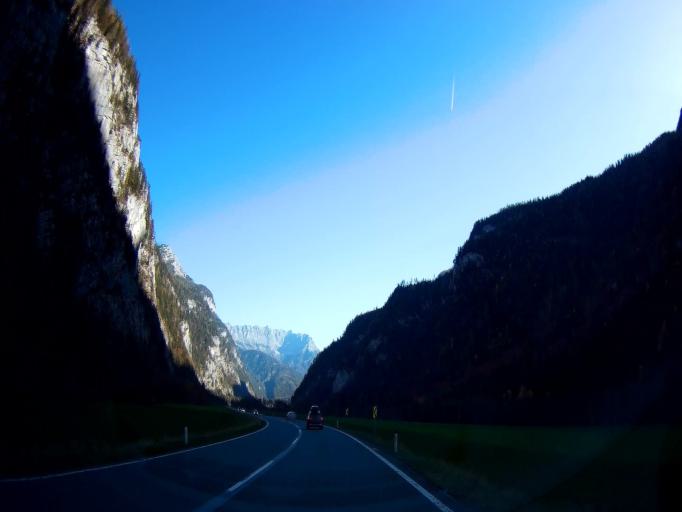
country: AT
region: Salzburg
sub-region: Politischer Bezirk Zell am See
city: Leogang
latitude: 47.5064
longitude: 12.7656
